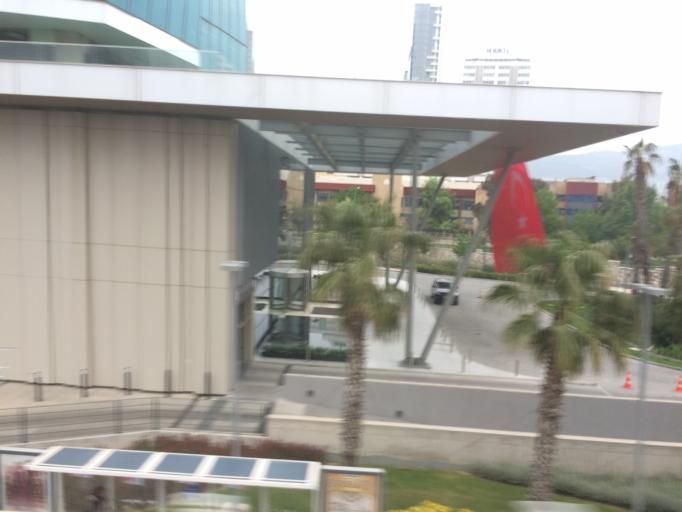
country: TR
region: Izmir
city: Buca
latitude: 38.4479
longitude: 27.1798
